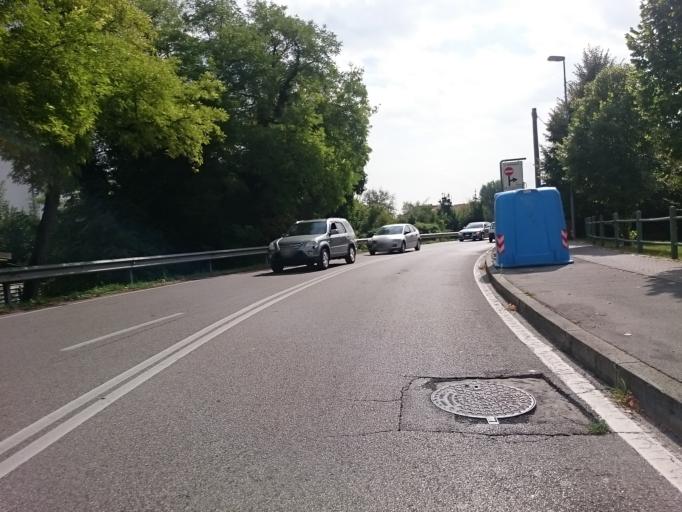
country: IT
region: Veneto
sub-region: Provincia di Padova
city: Padova
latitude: 45.4025
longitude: 11.9013
